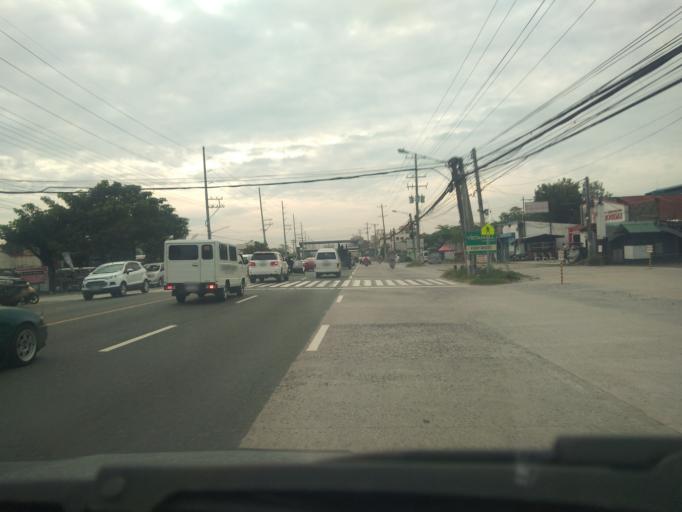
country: PH
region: Central Luzon
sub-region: Province of Pampanga
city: Magliman
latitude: 15.0549
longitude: 120.6606
